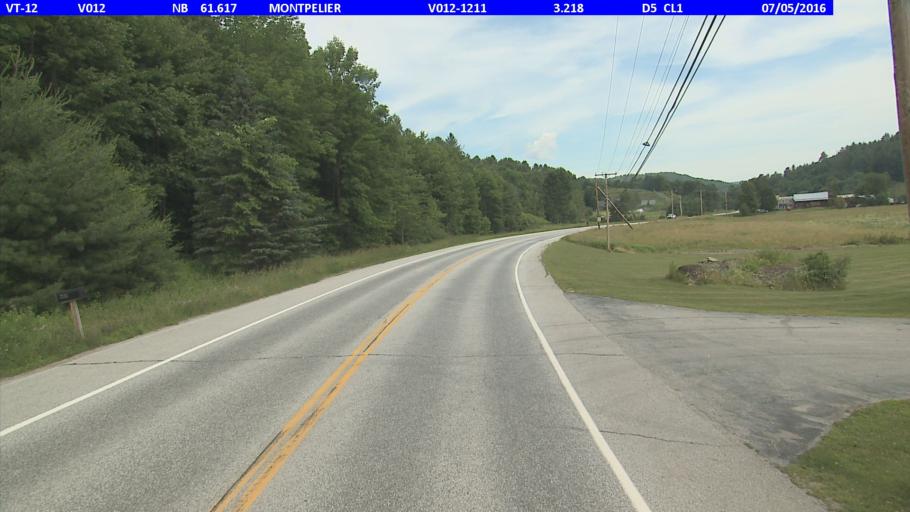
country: US
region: Vermont
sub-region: Washington County
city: Montpelier
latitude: 44.2881
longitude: -72.5789
